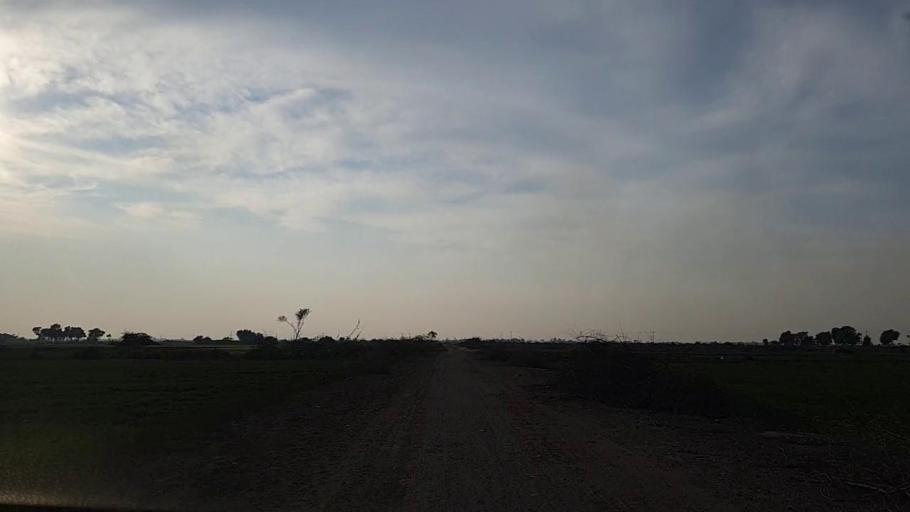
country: PK
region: Sindh
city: Bandhi
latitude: 26.5649
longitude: 68.2513
